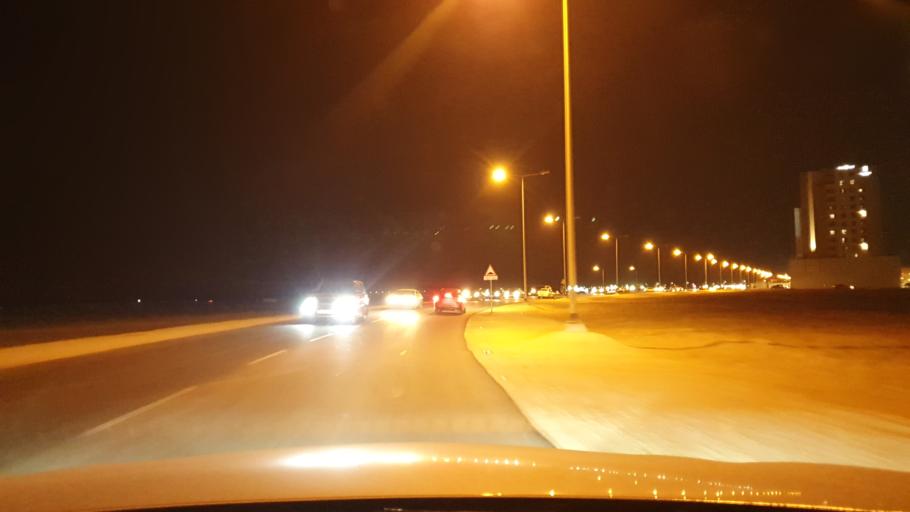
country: BH
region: Muharraq
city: Al Muharraq
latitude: 26.2607
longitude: 50.5950
